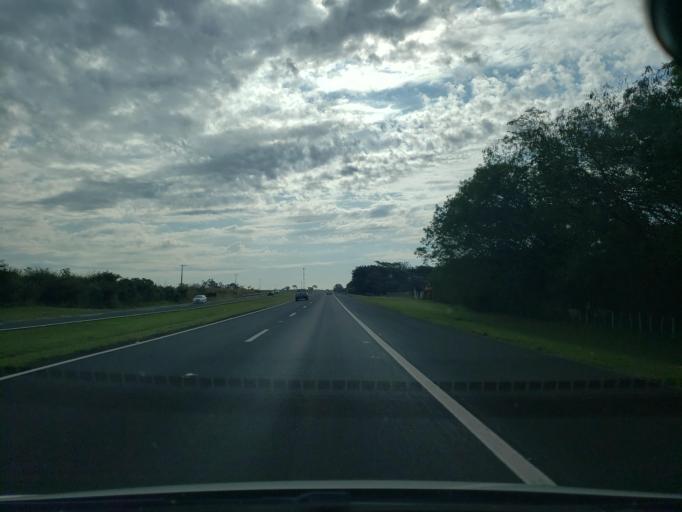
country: BR
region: Sao Paulo
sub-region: Birigui
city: Birigui
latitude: -21.3478
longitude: -50.3156
